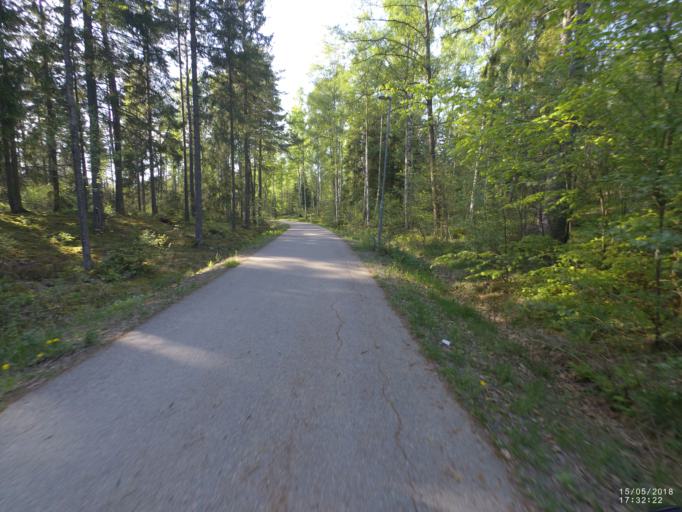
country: SE
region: Soedermanland
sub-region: Nykopings Kommun
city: Nykoping
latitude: 58.7353
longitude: 17.0128
